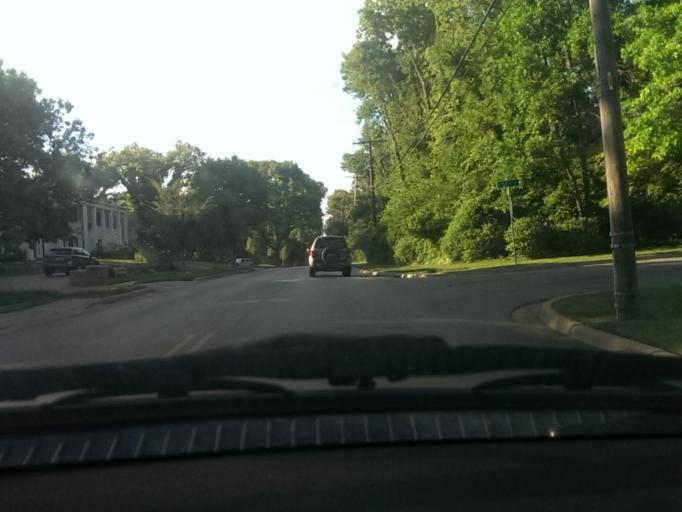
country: US
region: Kansas
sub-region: Johnson County
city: Mission Hills
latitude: 39.0246
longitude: -94.6076
